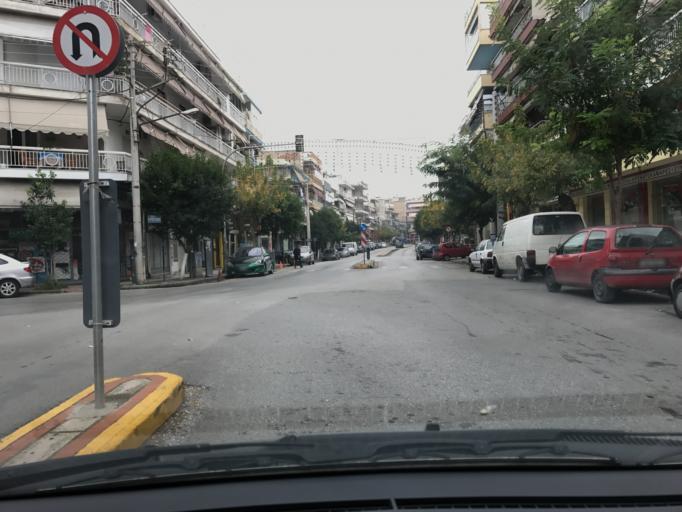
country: GR
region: Central Macedonia
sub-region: Nomos Thessalonikis
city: Ampelokipoi
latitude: 40.6500
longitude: 22.9292
